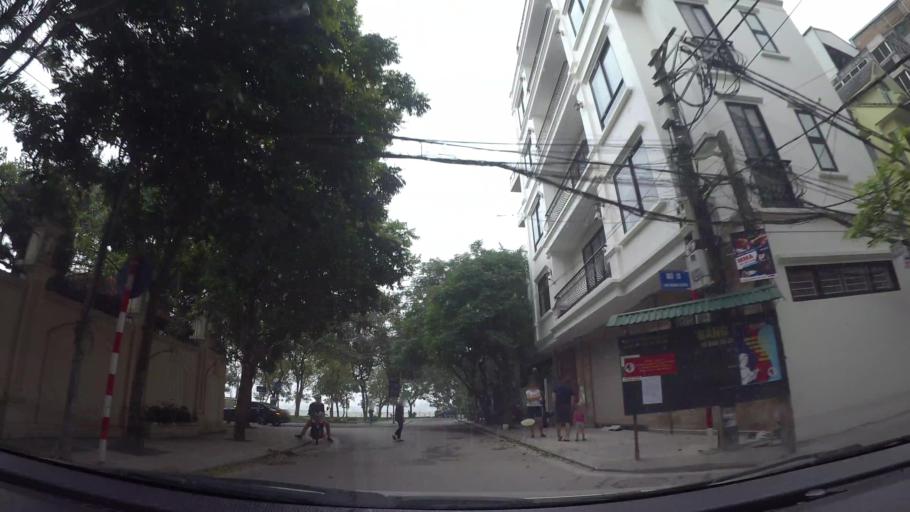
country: VN
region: Ha Noi
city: Tay Ho
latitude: 21.0559
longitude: 105.8211
